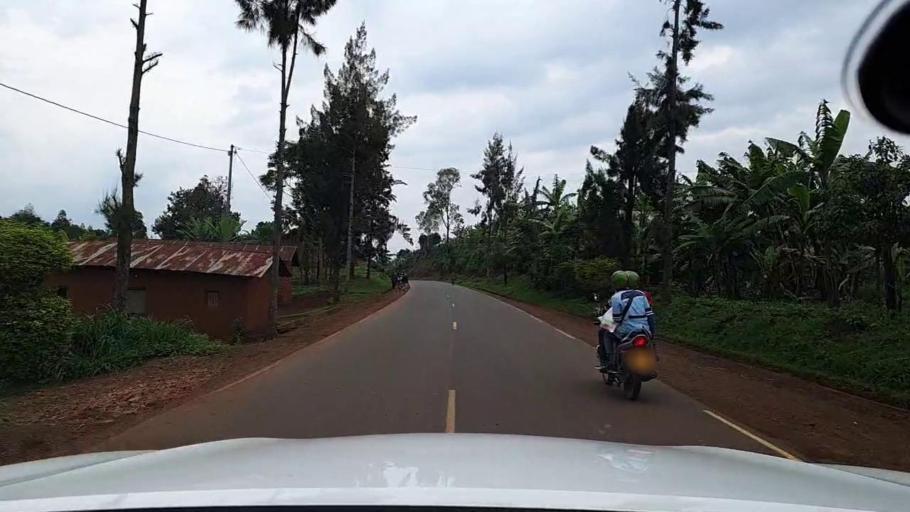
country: RW
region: Western Province
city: Cyangugu
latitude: -2.6087
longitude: 28.9353
